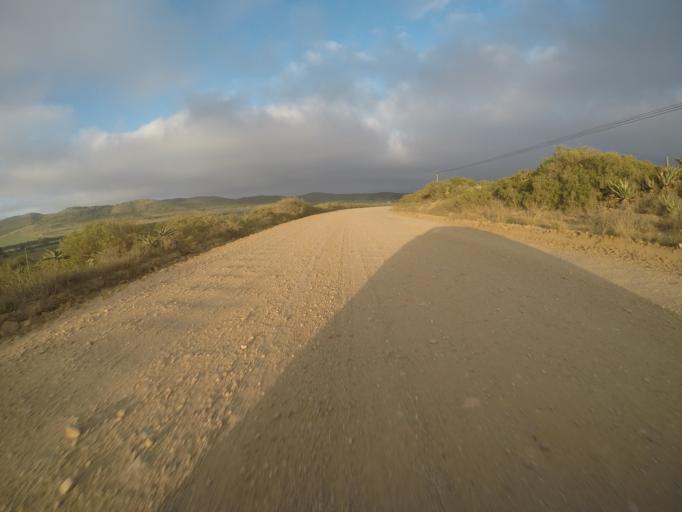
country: ZA
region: Western Cape
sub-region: Eden District Municipality
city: Mossel Bay
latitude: -34.1085
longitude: 22.0665
